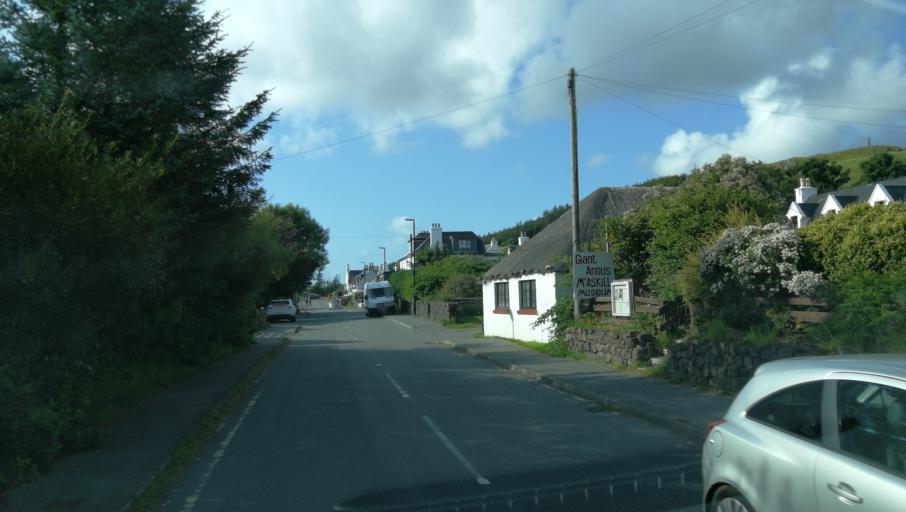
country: GB
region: Scotland
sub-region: Highland
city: Isle of Skye
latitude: 57.4352
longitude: -6.5792
